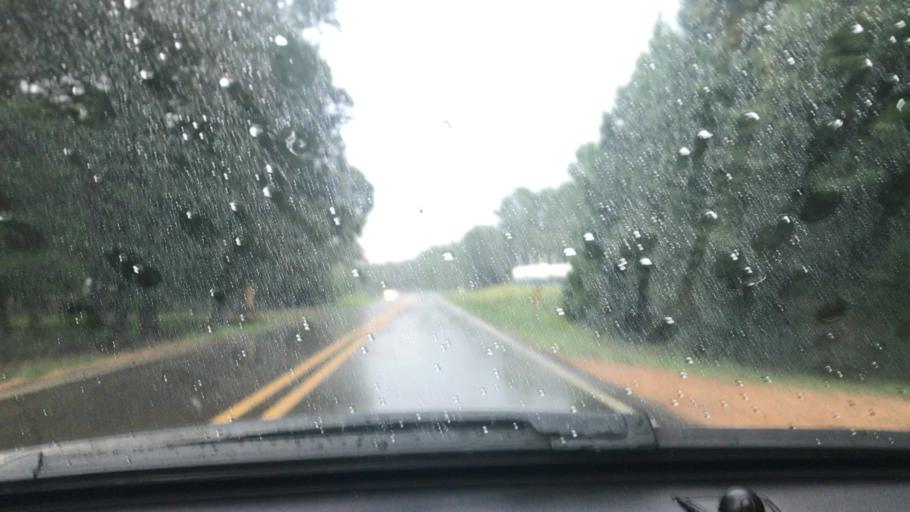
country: US
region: Mississippi
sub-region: Pike County
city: Summit
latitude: 31.3352
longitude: -90.5648
